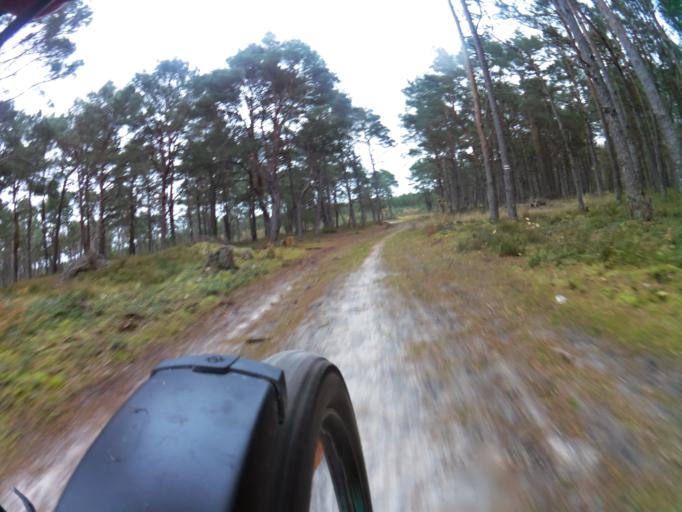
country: PL
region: Pomeranian Voivodeship
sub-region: Powiat leborski
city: Leba
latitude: 54.7783
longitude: 17.7149
